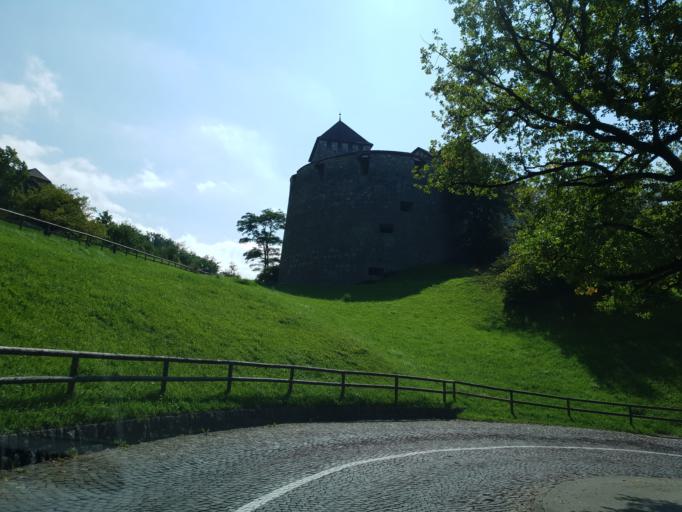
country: LI
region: Vaduz
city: Vaduz
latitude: 47.1406
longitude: 9.5246
